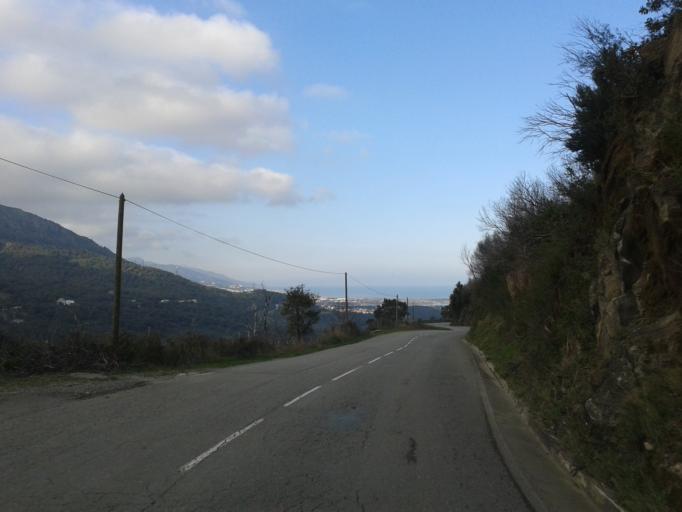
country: FR
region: Corsica
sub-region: Departement de la Haute-Corse
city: Biguglia
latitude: 42.5970
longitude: 9.4121
